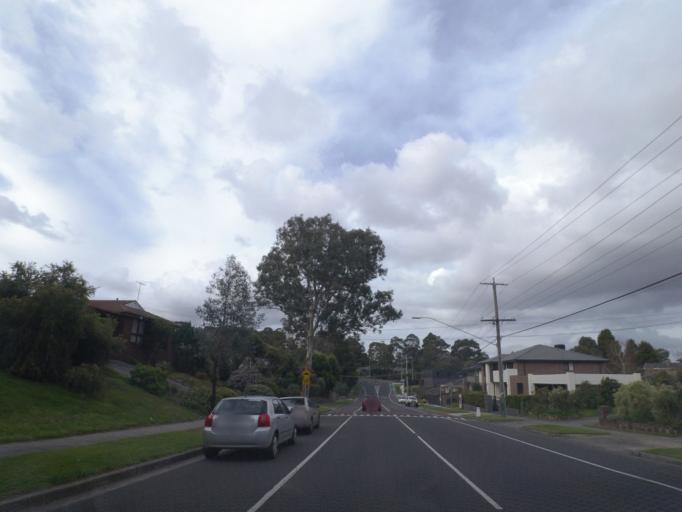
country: AU
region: Victoria
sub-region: Whitehorse
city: Vermont South
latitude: -37.8515
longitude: 145.1864
